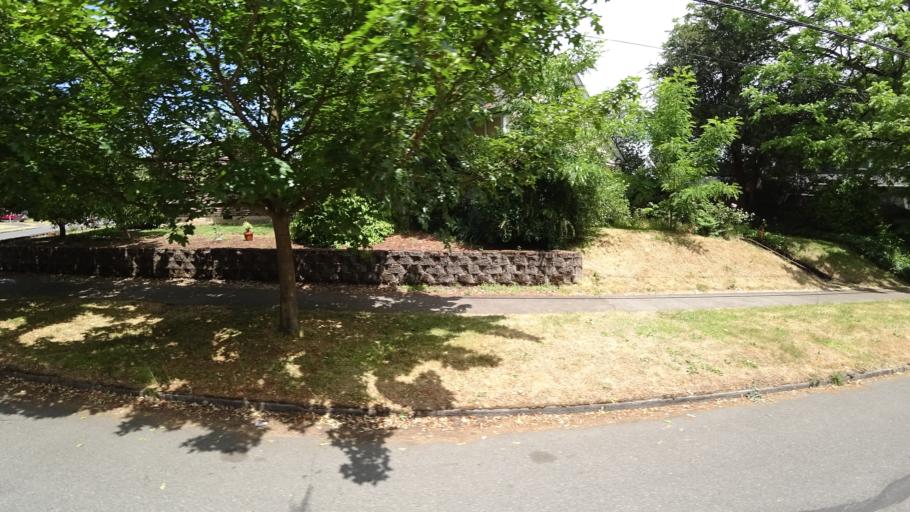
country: US
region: Oregon
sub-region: Washington County
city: West Haven
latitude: 45.5832
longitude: -122.7439
